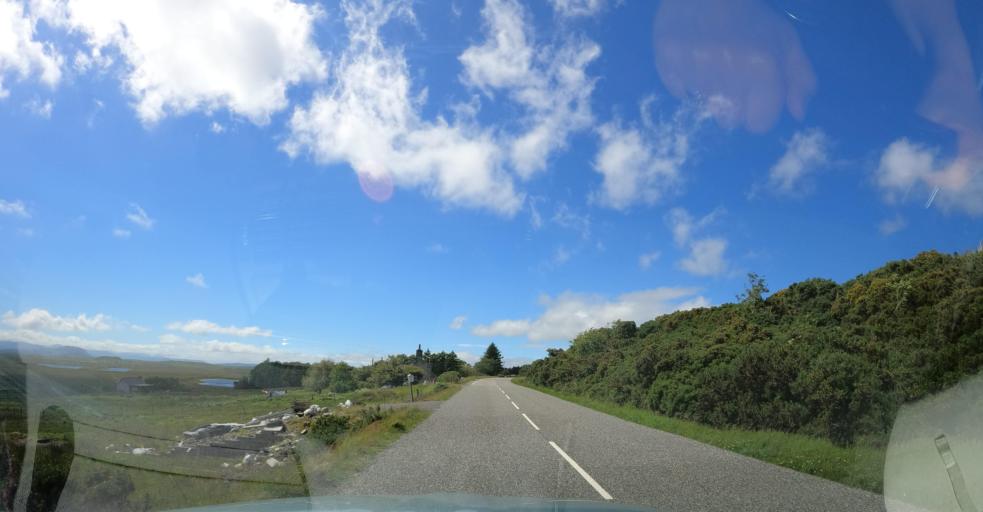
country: GB
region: Scotland
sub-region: Eilean Siar
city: Stornoway
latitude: 58.1658
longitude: -6.5581
